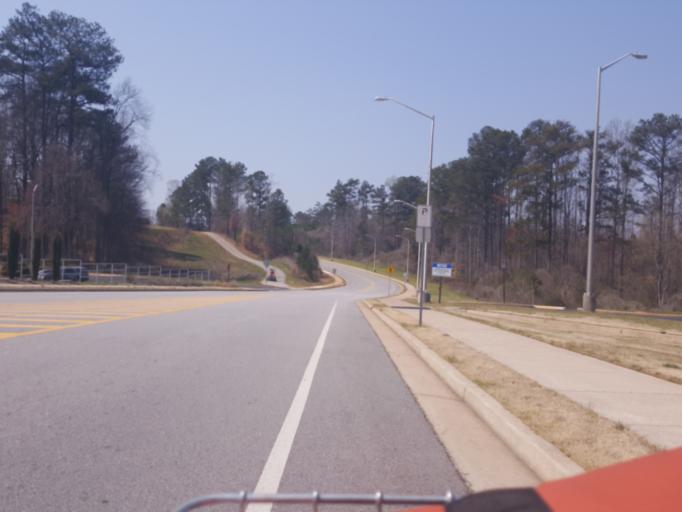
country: US
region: Georgia
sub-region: Carroll County
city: Carrollton
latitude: 33.5750
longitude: -85.1047
